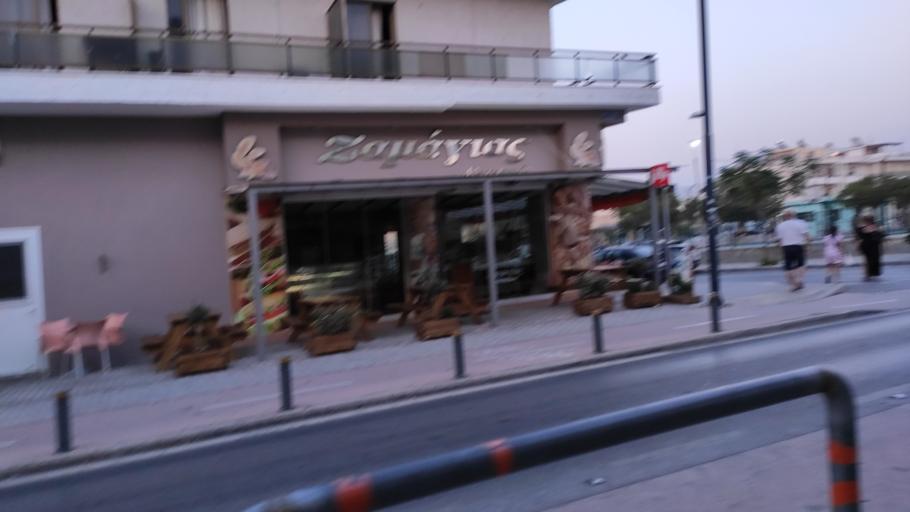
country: GR
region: South Aegean
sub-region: Nomos Dodekanisou
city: Kos
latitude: 36.9009
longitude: 27.2827
